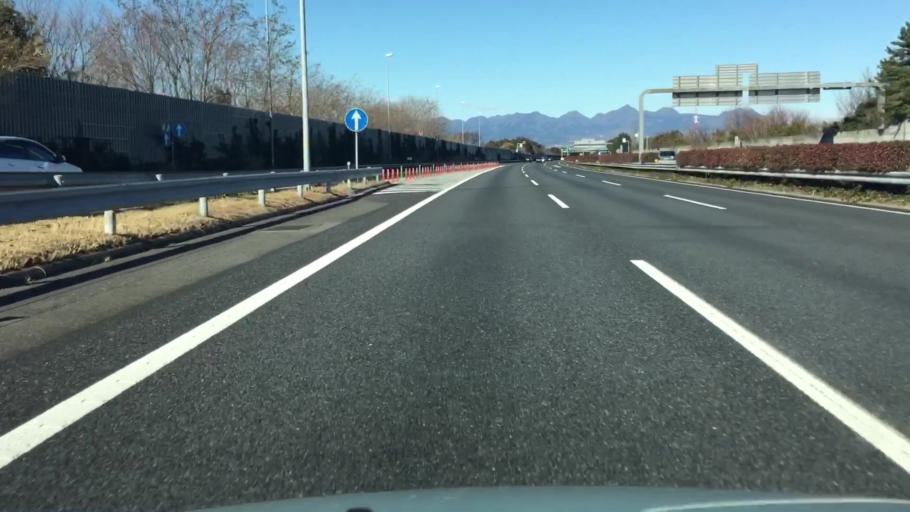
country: JP
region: Gunma
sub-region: Sawa-gun
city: Tamamura
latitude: 36.3231
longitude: 139.0718
